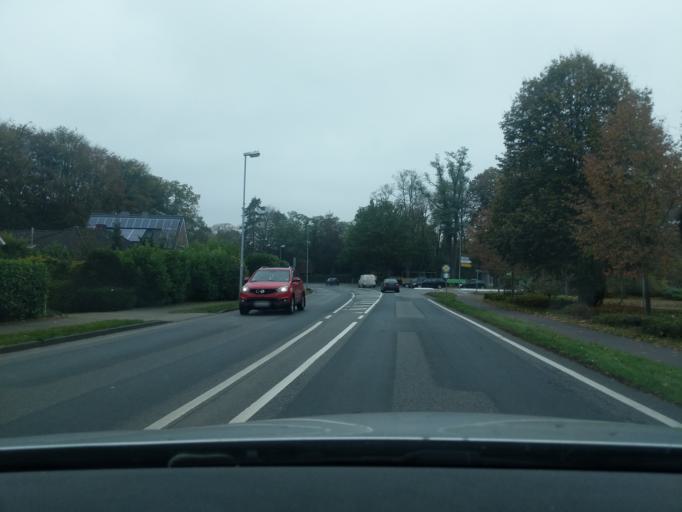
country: DE
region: Lower Saxony
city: Himmelpforten
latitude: 53.6116
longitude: 9.3131
